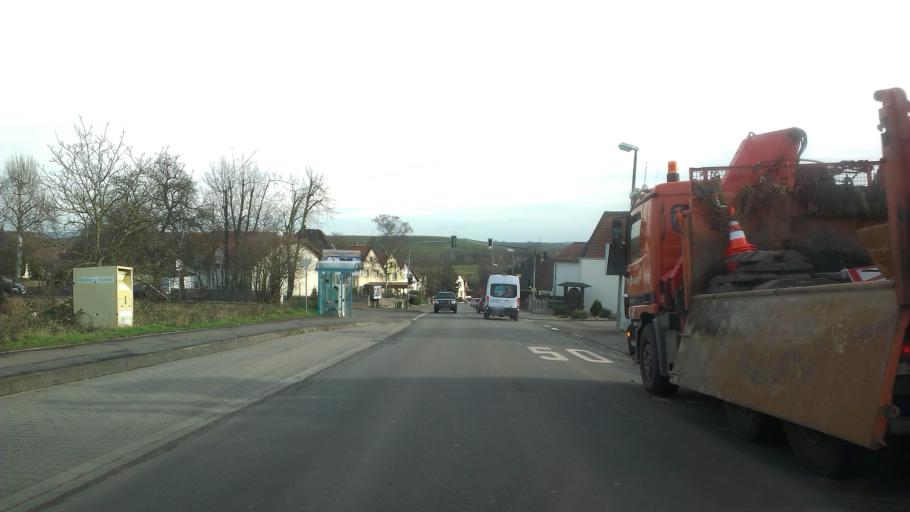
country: DE
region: Rheinland-Pfalz
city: Hackenheim
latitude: 49.8262
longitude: 7.8972
